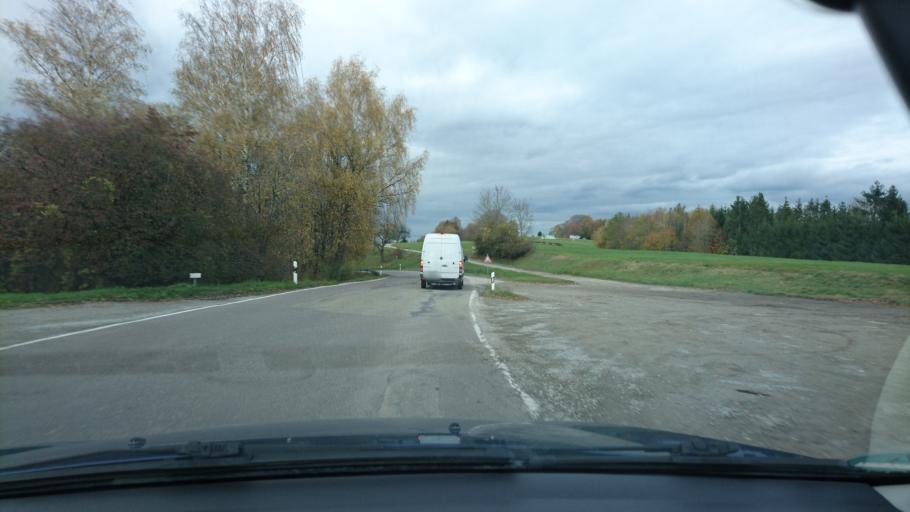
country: DE
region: Baden-Wuerttemberg
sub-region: Regierungsbezirk Stuttgart
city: Gschwend
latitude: 48.9352
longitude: 9.7896
